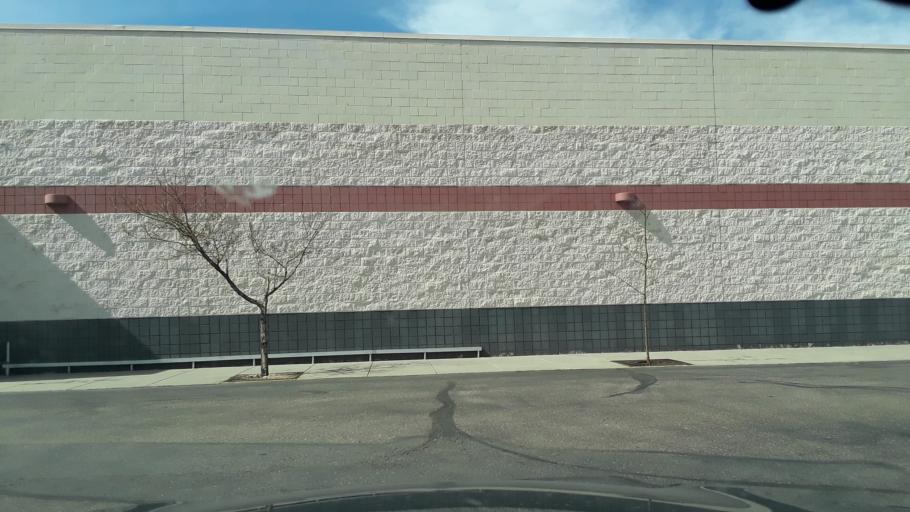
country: US
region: Colorado
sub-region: El Paso County
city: Air Force Academy
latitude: 38.9337
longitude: -104.7933
